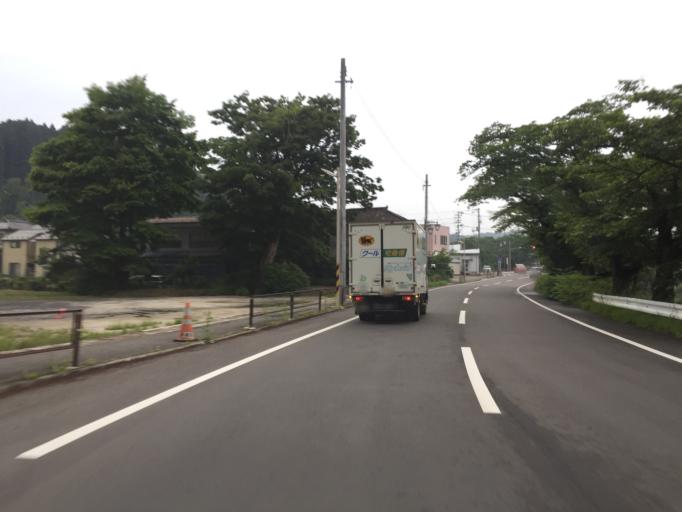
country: JP
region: Fukushima
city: Ishikawa
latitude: 37.1463
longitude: 140.4524
